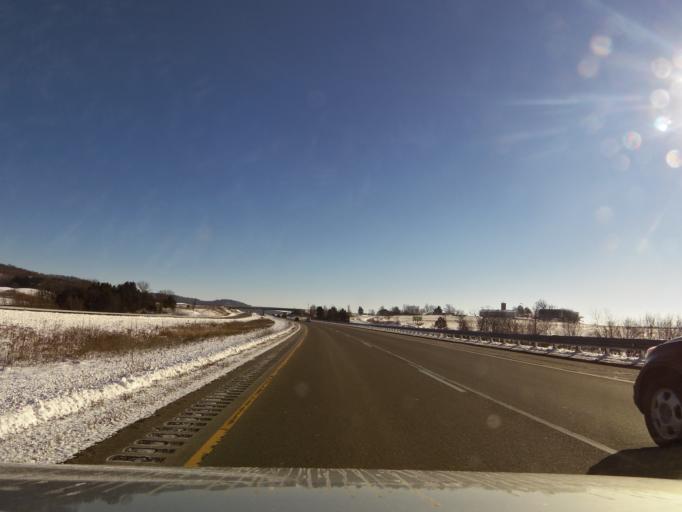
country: US
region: Wisconsin
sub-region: Trempealeau County
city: Blair
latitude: 44.4131
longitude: -91.0453
